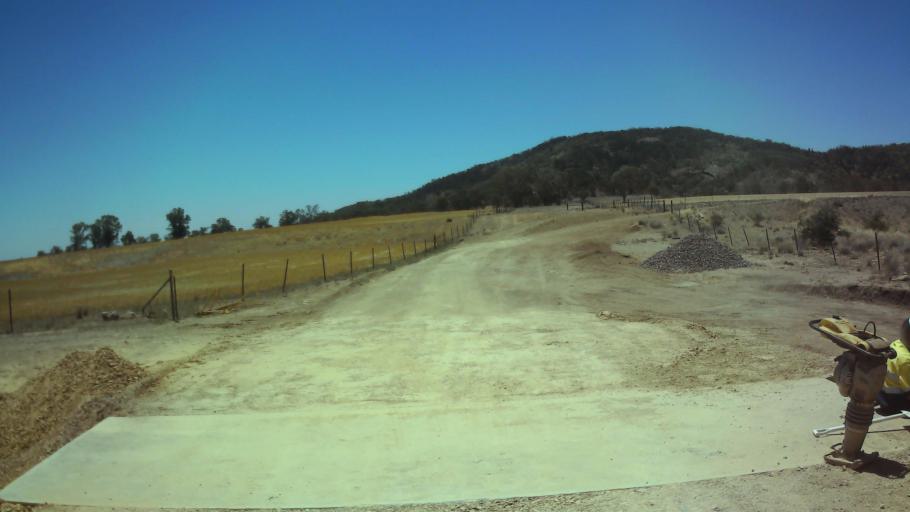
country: AU
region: New South Wales
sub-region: Weddin
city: Grenfell
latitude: -33.8539
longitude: 148.1081
